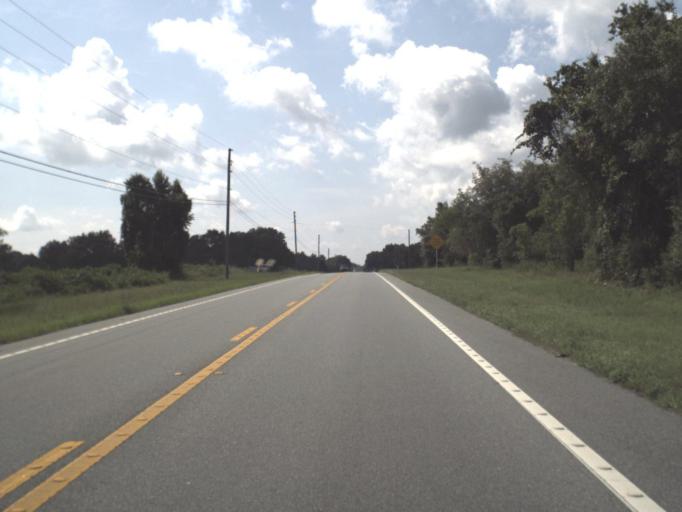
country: US
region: Florida
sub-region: Citrus County
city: Beverly Hills
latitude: 28.9559
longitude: -82.4127
